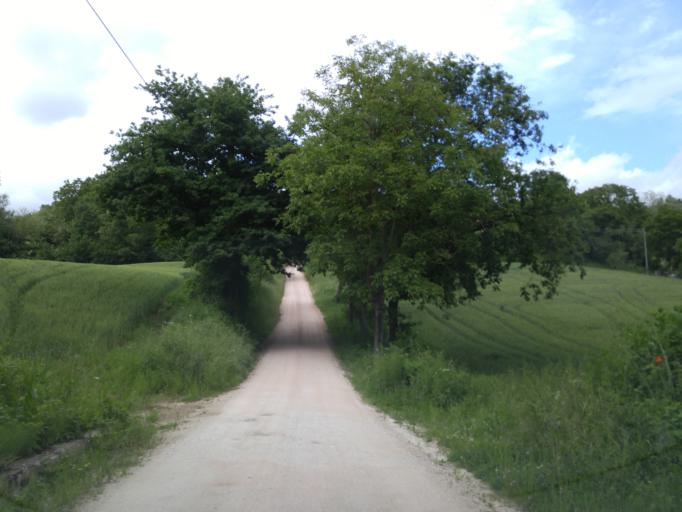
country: IT
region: The Marches
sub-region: Provincia di Pesaro e Urbino
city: Urbino
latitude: 43.7060
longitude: 12.6323
